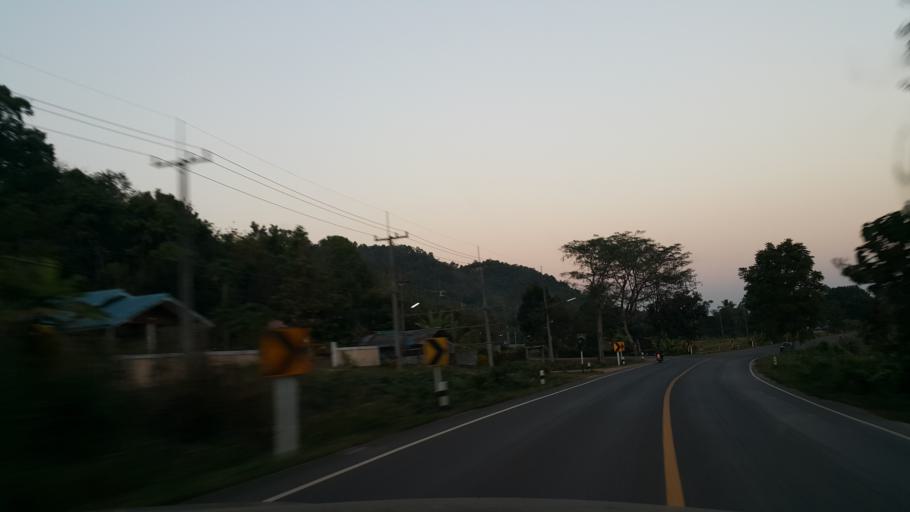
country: TH
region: Phrae
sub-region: Amphoe Wang Chin
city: Wang Chin
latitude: 17.9731
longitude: 99.6239
